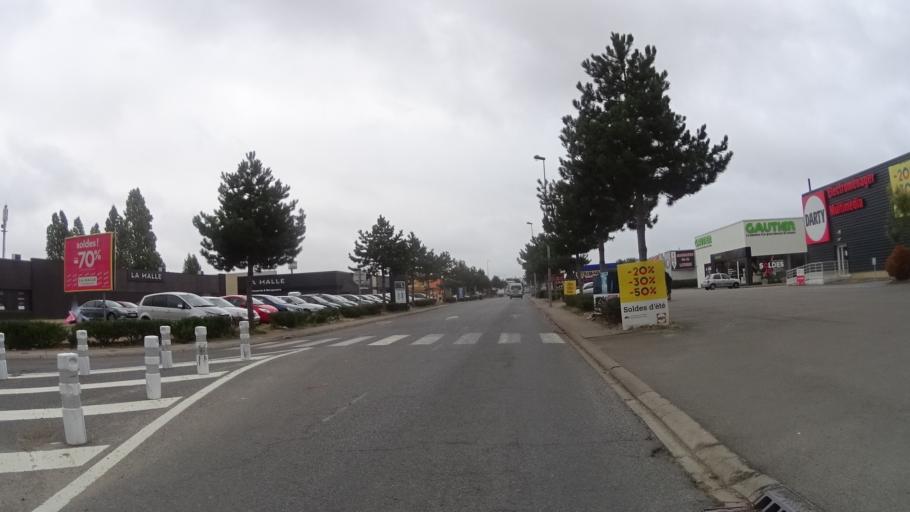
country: FR
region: Pays de la Loire
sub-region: Departement de la Loire-Atlantique
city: Saint-Nazaire
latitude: 47.3006
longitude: -2.2124
